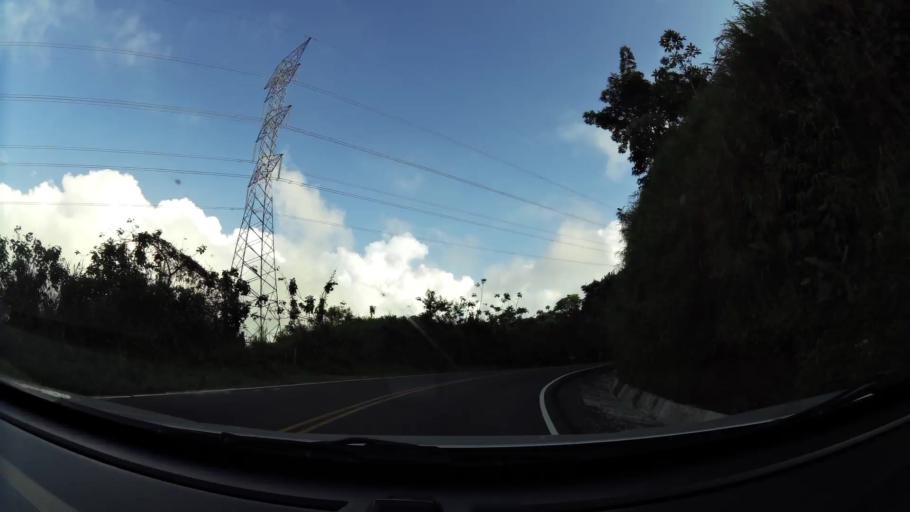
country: CR
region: Limon
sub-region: Canton de Siquirres
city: Siquirres
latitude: 10.0508
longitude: -83.5500
